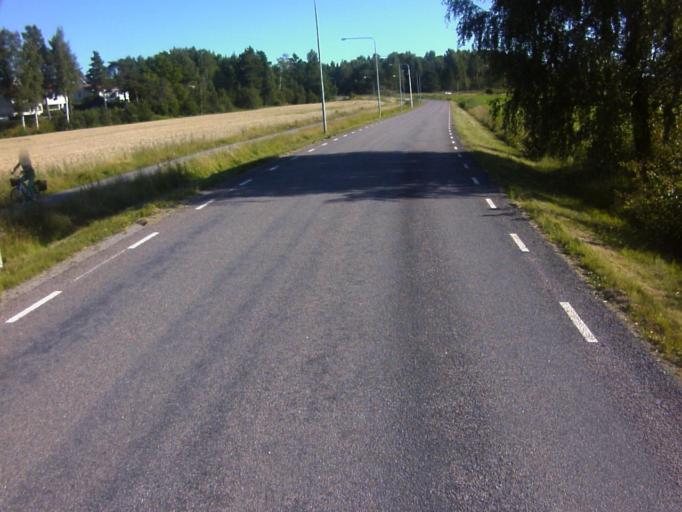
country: SE
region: Soedermanland
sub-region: Eskilstuna Kommun
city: Hallbybrunn
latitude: 59.3847
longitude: 16.4271
